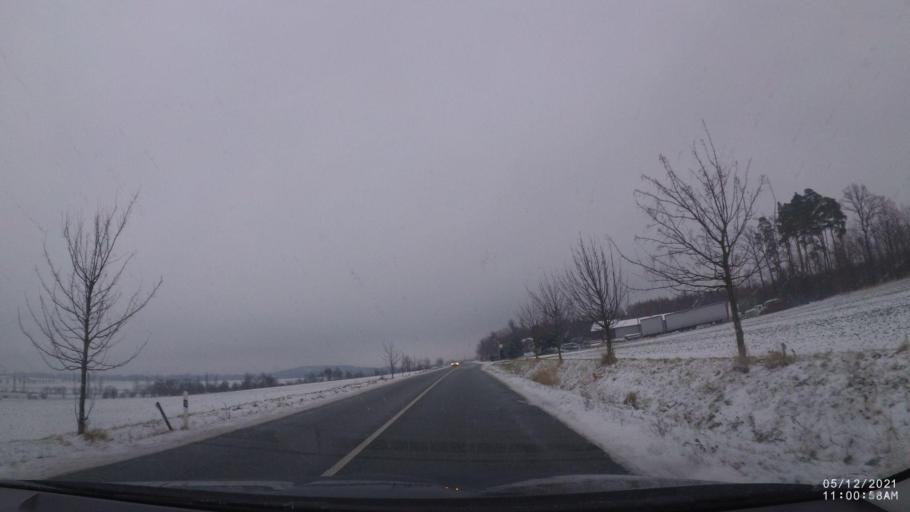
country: CZ
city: Solnice
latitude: 50.1693
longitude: 16.2205
